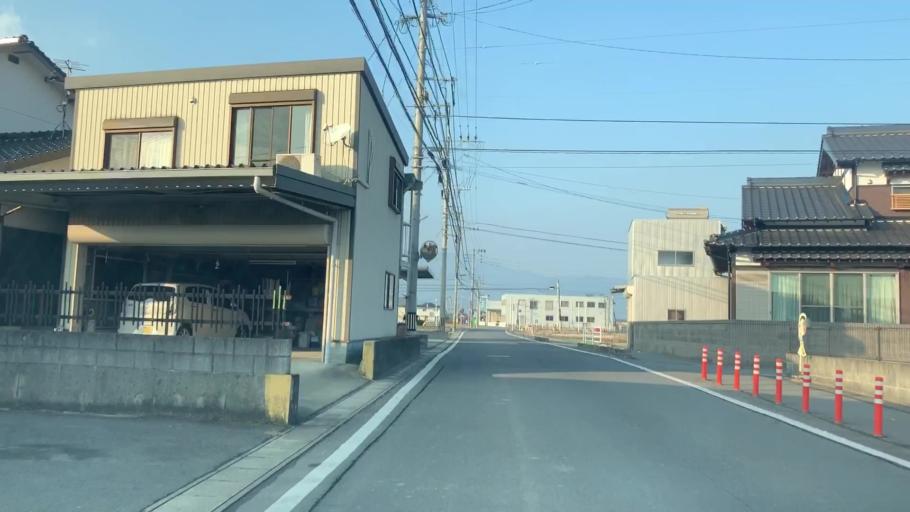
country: JP
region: Saga Prefecture
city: Saga-shi
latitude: 33.2657
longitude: 130.2307
